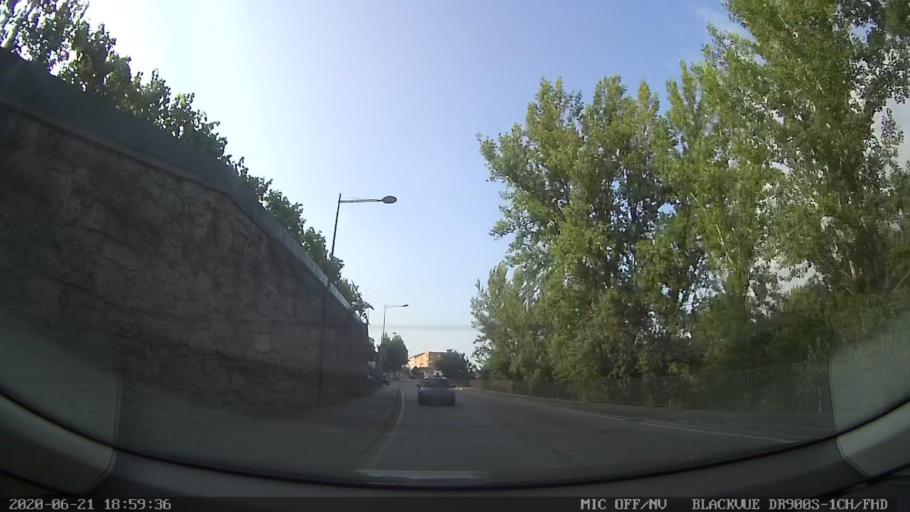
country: PT
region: Porto
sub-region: Amarante
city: Amarante
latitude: 41.2762
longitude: -8.0821
